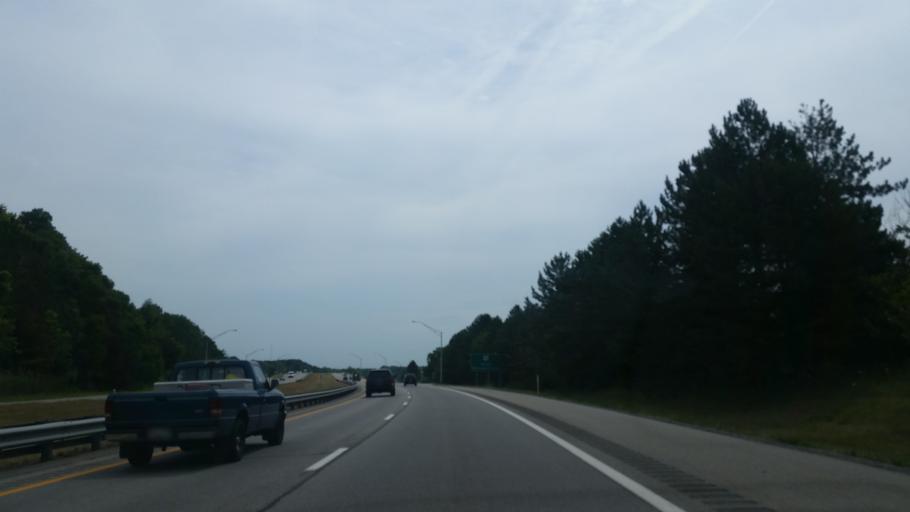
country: US
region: Ohio
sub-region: Cuyahoga County
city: Solon
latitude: 41.3947
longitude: -81.4456
